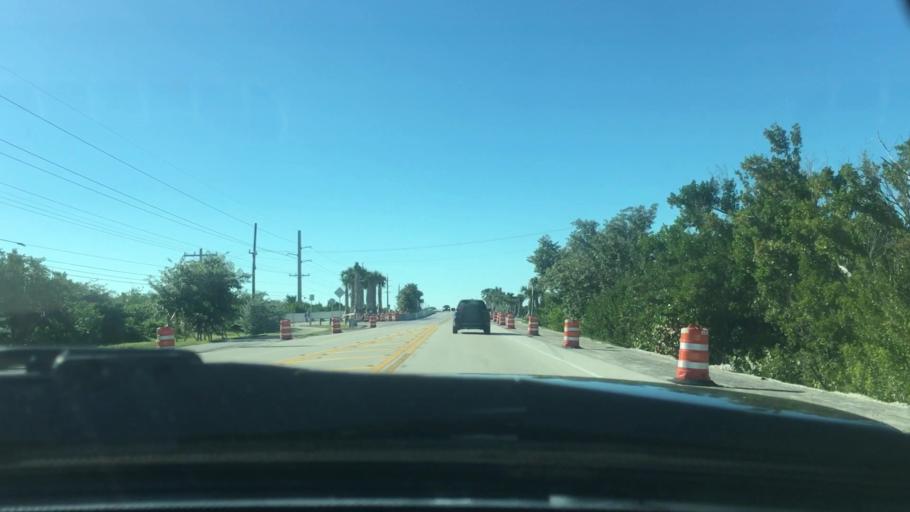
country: US
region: Florida
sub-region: Monroe County
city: Cudjoe Key
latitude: 24.6633
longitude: -81.4638
